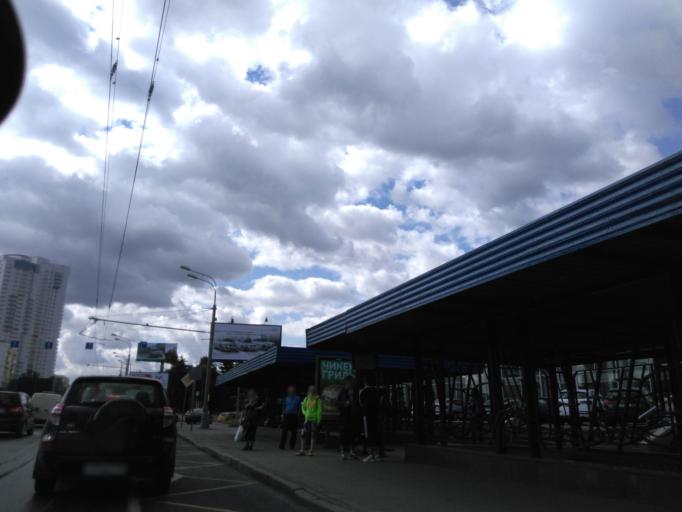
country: RU
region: Moskovskaya
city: Levoberezhnyy
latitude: 55.8642
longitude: 37.4639
